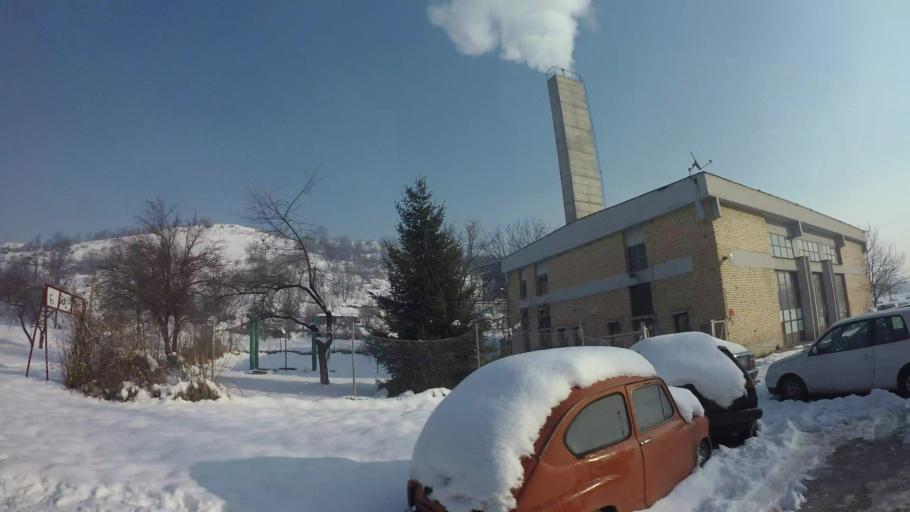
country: BA
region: Federation of Bosnia and Herzegovina
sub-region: Kanton Sarajevo
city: Sarajevo
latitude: 43.8329
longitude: 18.3460
